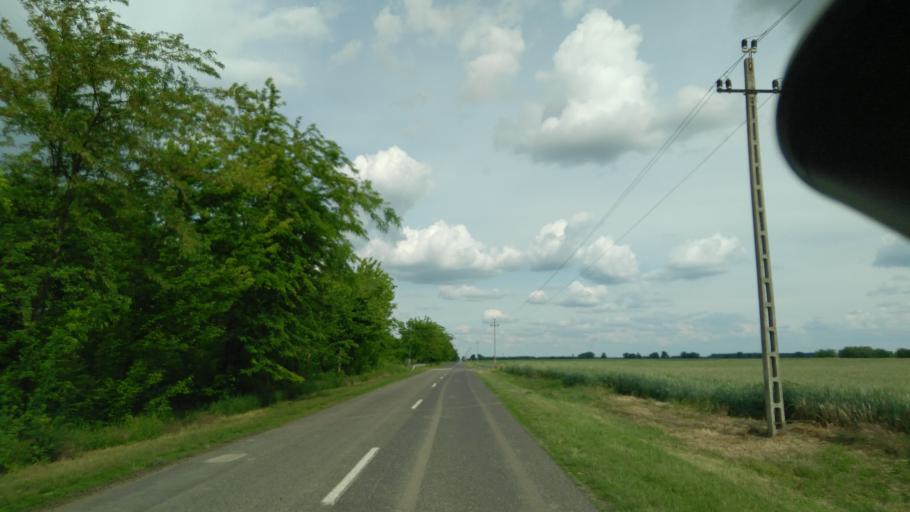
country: HU
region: Bekes
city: Mezohegyes
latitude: 46.3076
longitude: 20.8854
